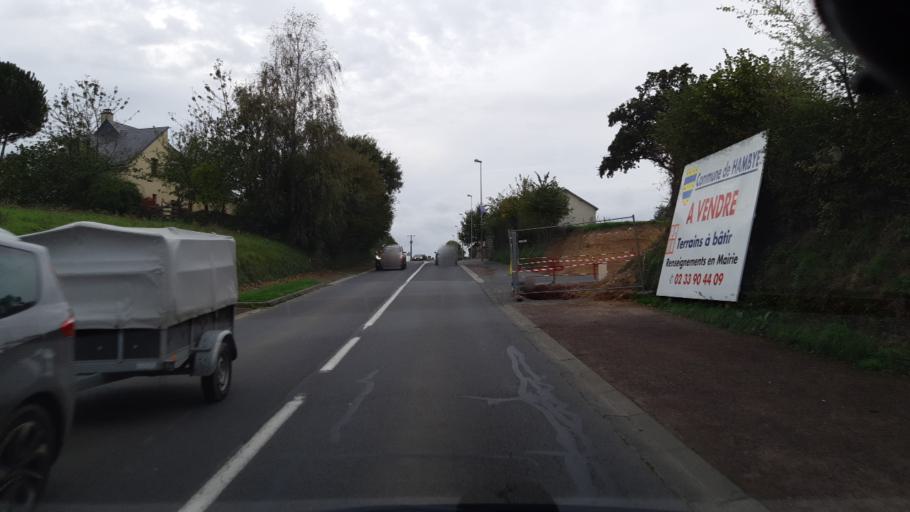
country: FR
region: Lower Normandy
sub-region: Departement de la Manche
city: Hambye
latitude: 48.9469
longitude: -1.2756
